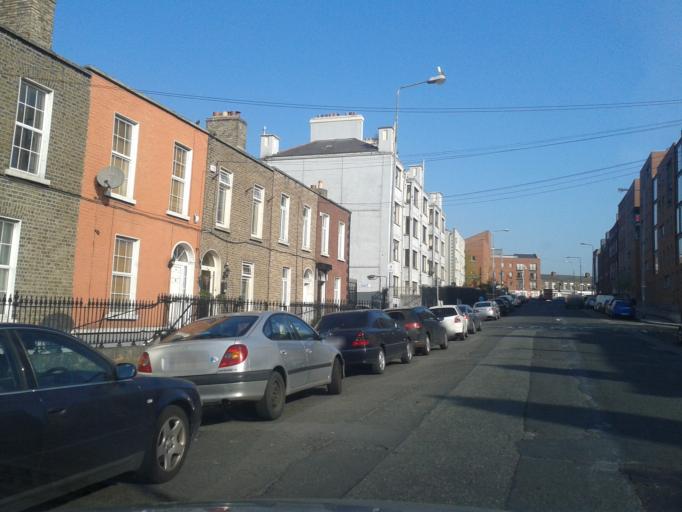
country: IE
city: Fairview
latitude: 53.3548
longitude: -6.2500
